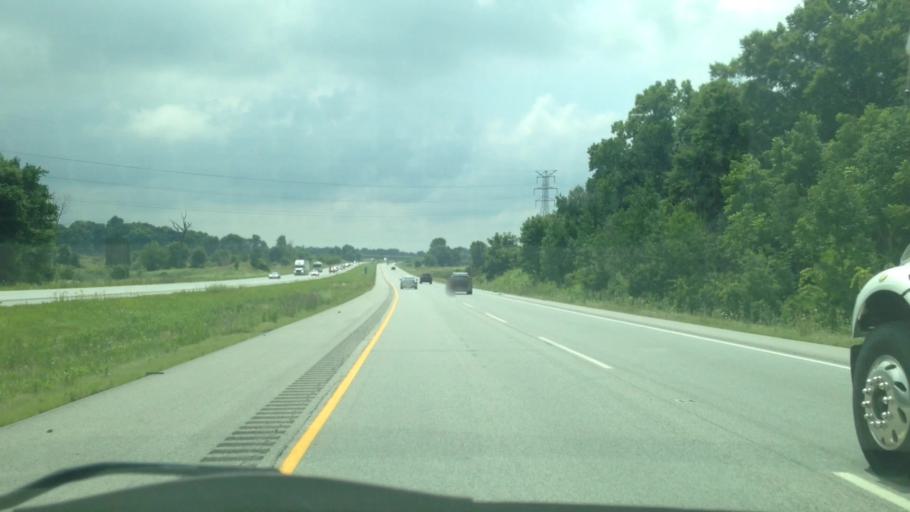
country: US
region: Indiana
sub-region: LaPorte County
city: LaPorte
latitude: 41.6495
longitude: -86.7714
